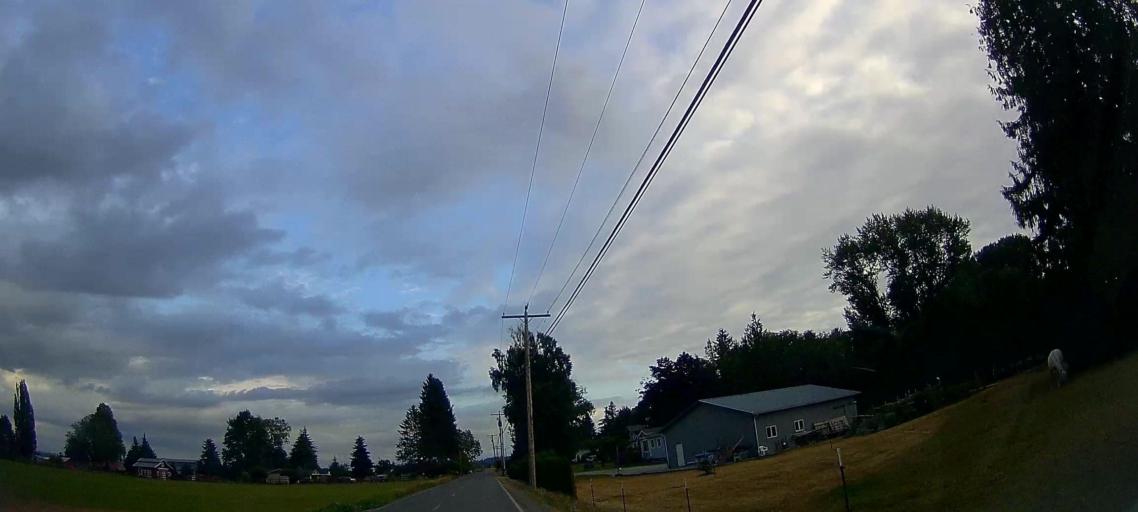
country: US
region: Washington
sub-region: Skagit County
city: Burlington
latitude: 48.5329
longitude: -122.4114
